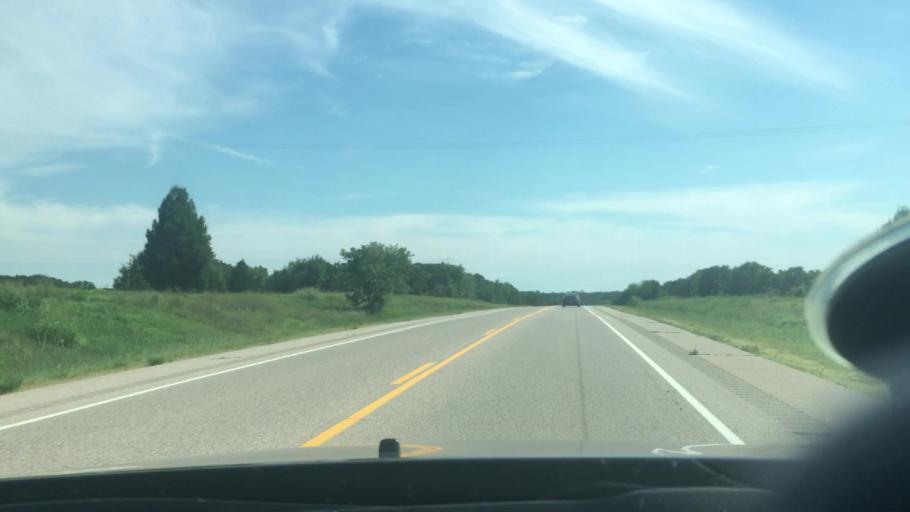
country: US
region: Oklahoma
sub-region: Seminole County
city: Maud
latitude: 35.0693
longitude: -96.6789
